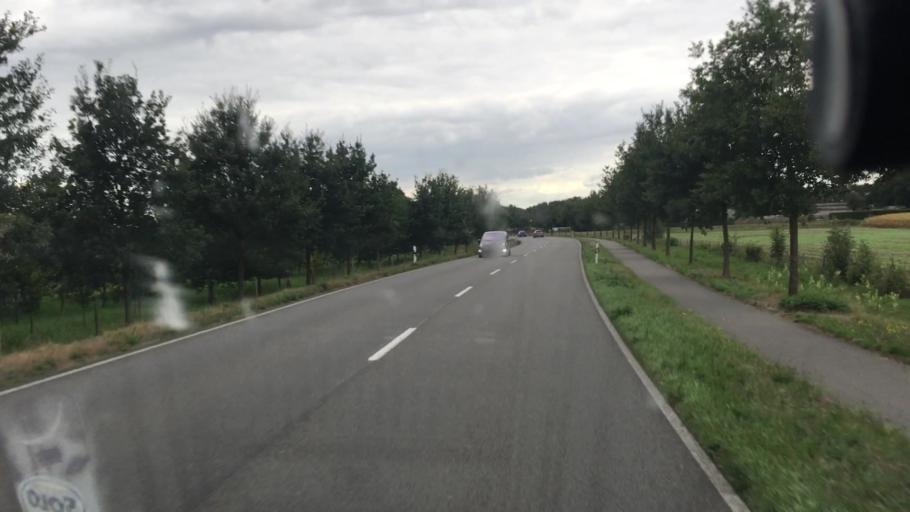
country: DE
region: Lower Saxony
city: Lohne
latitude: 52.6528
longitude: 8.2018
